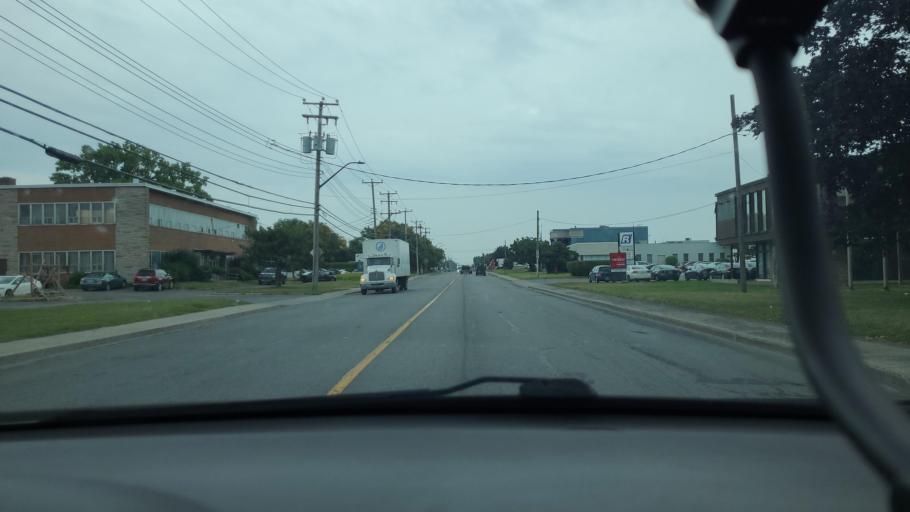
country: CA
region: Quebec
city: Saint-Laurent
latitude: 45.4846
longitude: -73.7153
